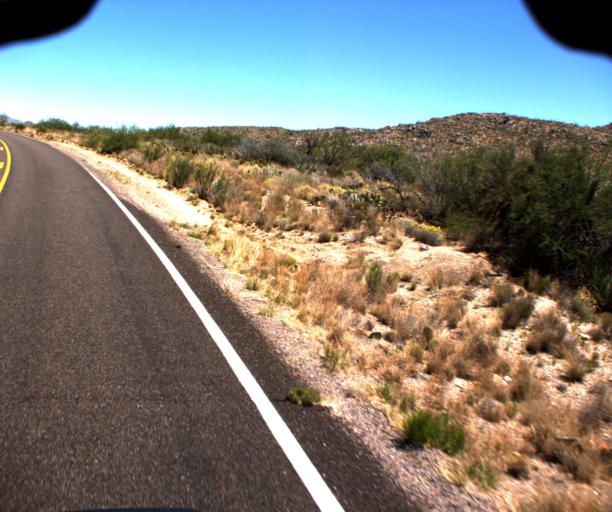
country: US
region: Arizona
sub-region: Yavapai County
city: Bagdad
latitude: 34.5062
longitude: -113.1542
